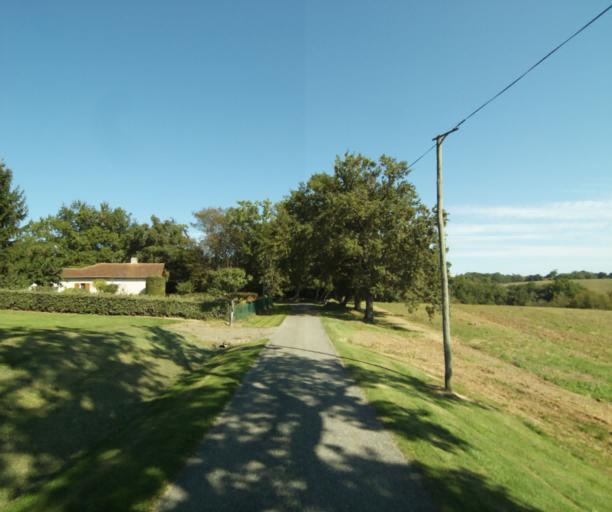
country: FR
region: Midi-Pyrenees
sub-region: Departement du Gers
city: Cazaubon
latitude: 43.9444
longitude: -0.0217
